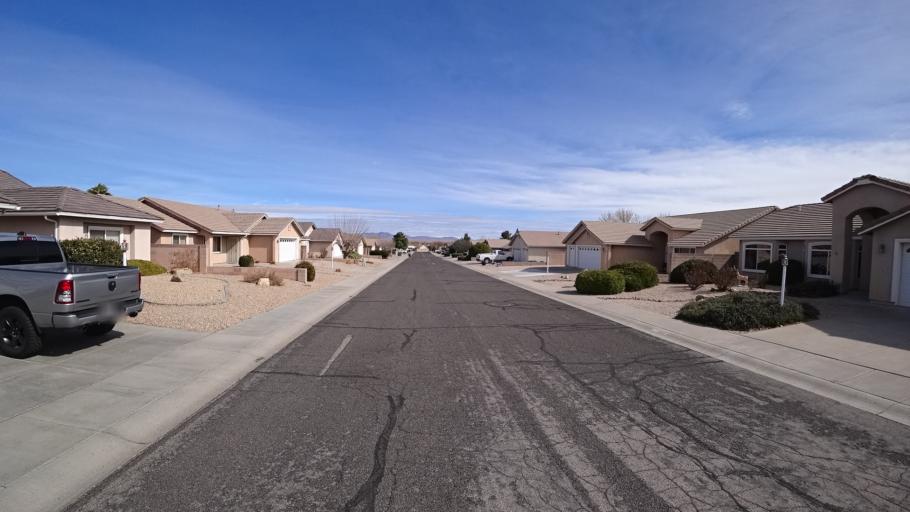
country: US
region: Arizona
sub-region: Mohave County
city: New Kingman-Butler
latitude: 35.2347
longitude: -114.0329
